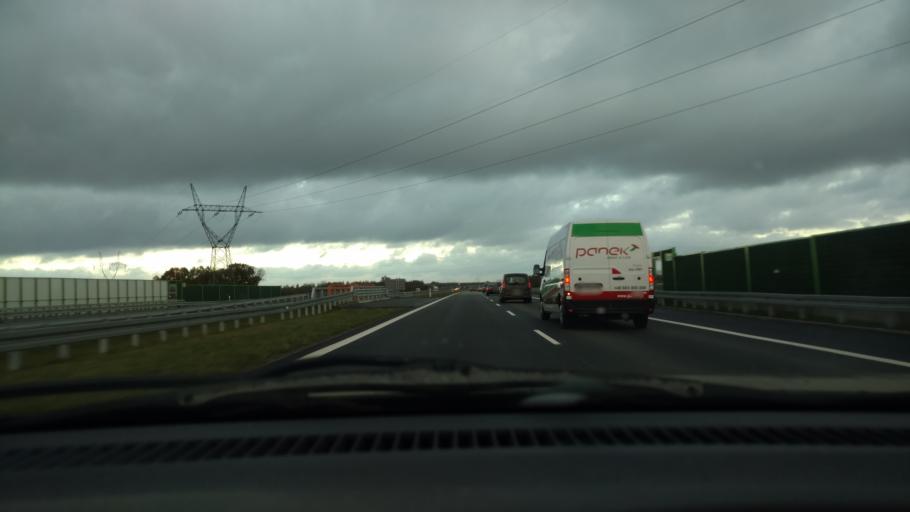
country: PL
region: Lodz Voivodeship
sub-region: Powiat lodzki wschodni
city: Brojce
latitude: 51.6898
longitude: 19.5974
